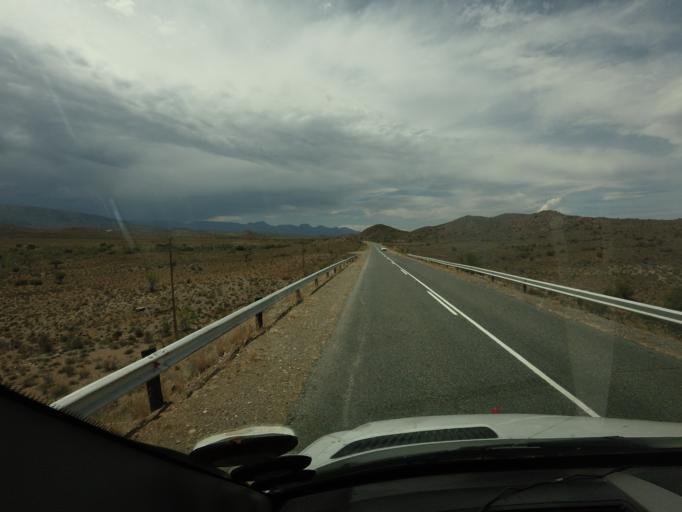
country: ZA
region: Western Cape
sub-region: Eden District Municipality
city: Ladismith
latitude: -33.6344
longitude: 21.0399
